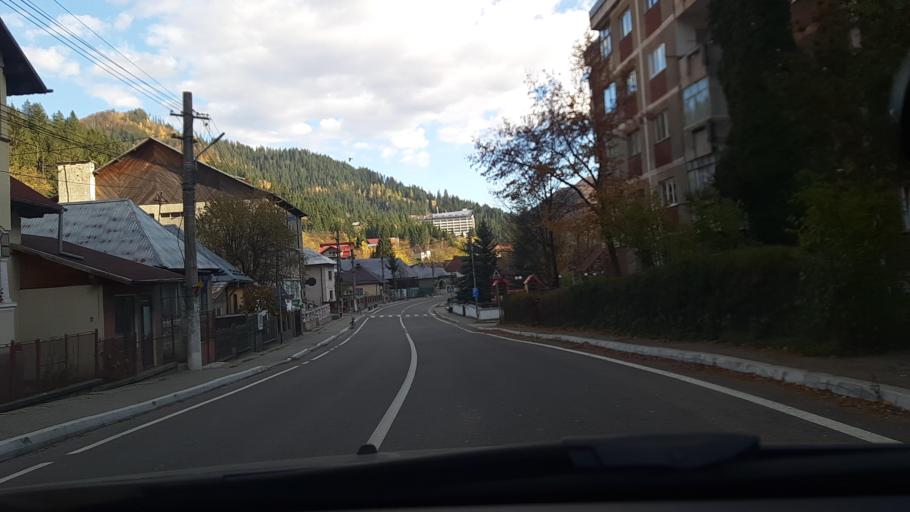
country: RO
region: Valcea
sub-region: Comuna Voineasa
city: Voineasa
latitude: 45.4200
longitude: 23.9554
